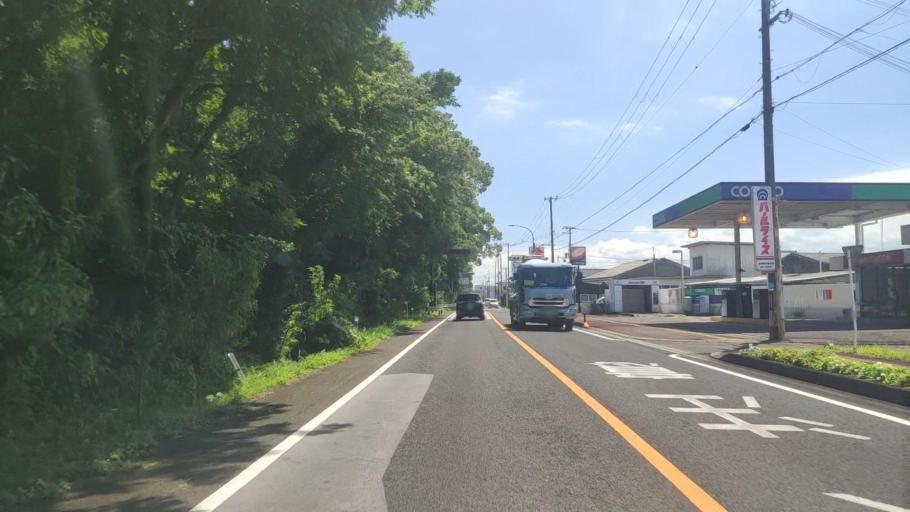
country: JP
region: Wakayama
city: Shingu
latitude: 33.8715
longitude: 136.0851
